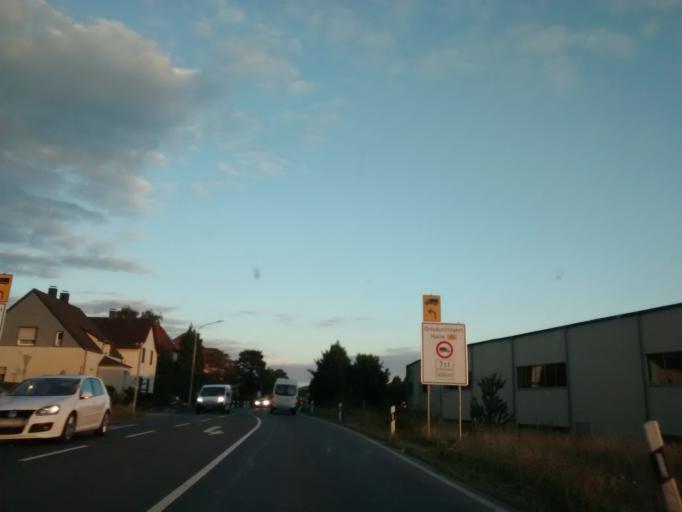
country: DE
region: North Rhine-Westphalia
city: Halle
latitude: 52.0690
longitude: 8.3424
